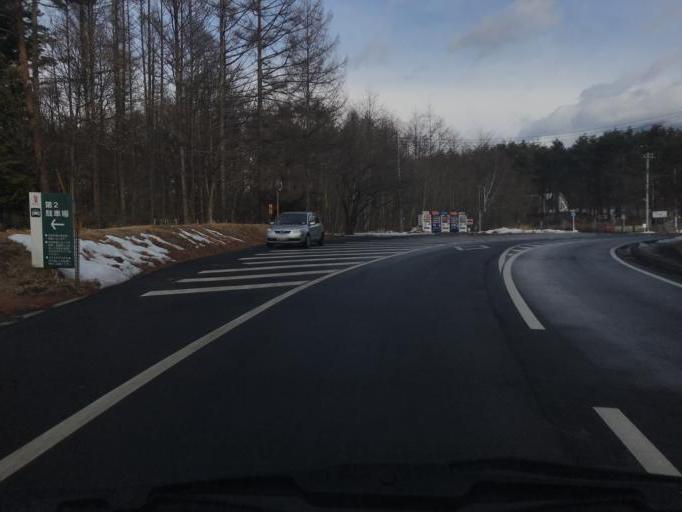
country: JP
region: Nagano
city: Chino
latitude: 35.8820
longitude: 138.3086
